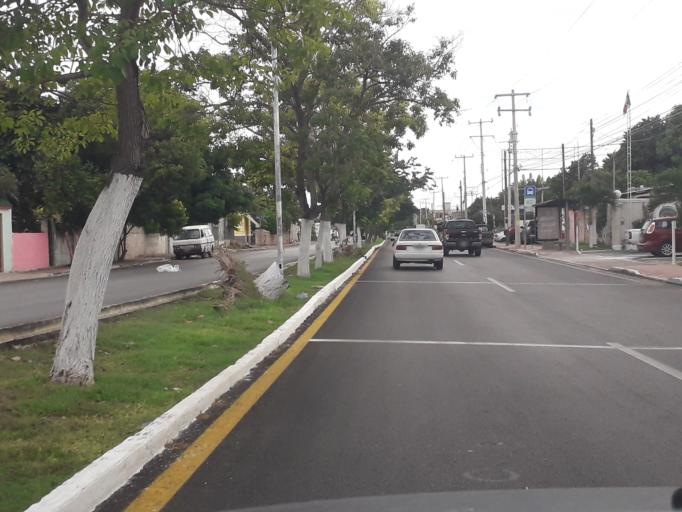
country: MX
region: Yucatan
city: Merida
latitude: 20.9697
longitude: -89.6636
